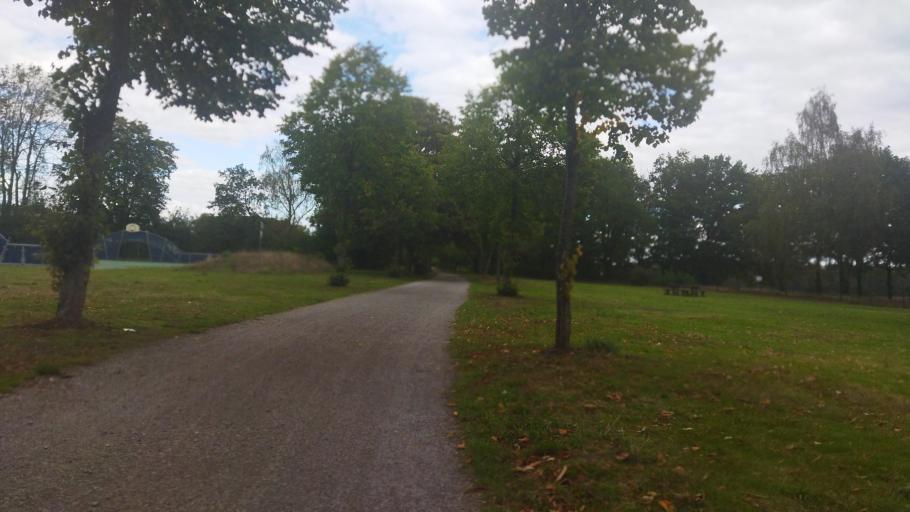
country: DE
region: North Rhine-Westphalia
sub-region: Regierungsbezirk Munster
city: Haltern
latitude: 51.7460
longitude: 7.2009
